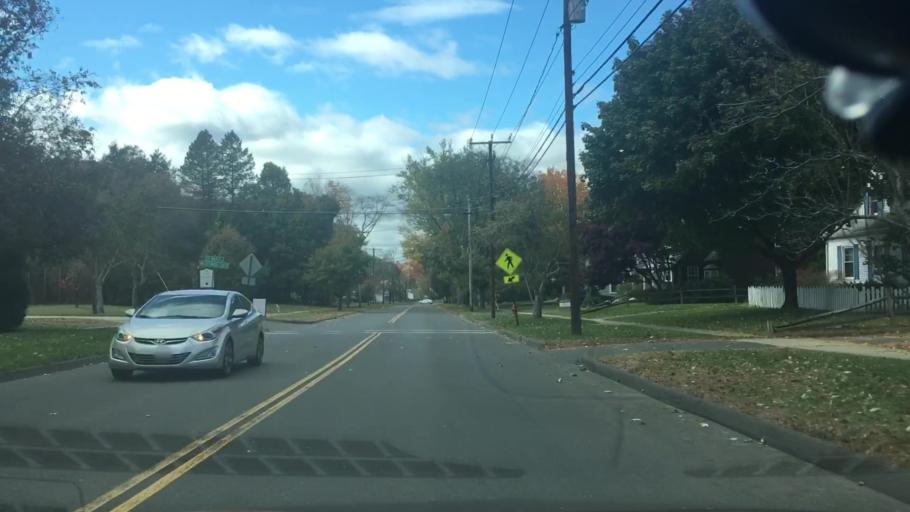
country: US
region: Massachusetts
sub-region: Hampden County
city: Longmeadow
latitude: 42.0320
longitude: -72.5734
